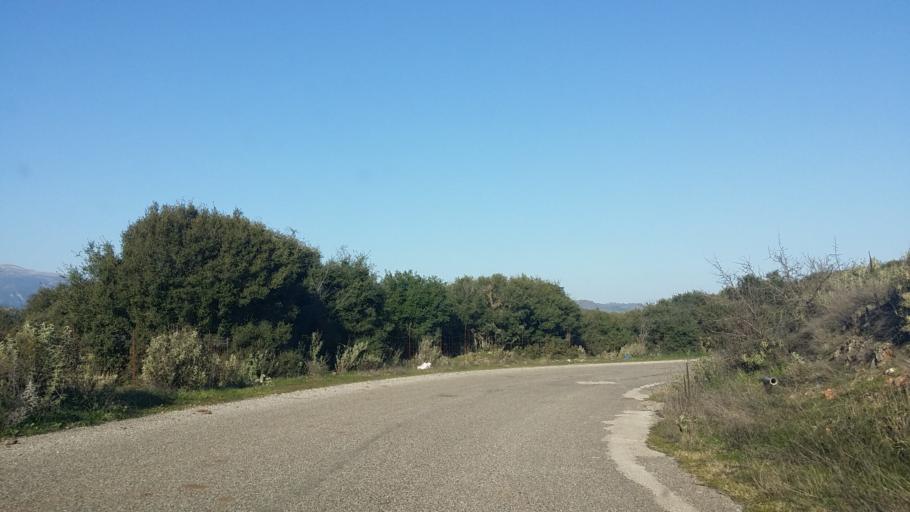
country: GR
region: West Greece
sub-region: Nomos Aitolias kai Akarnanias
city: Katouna
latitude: 38.7684
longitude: 21.1339
